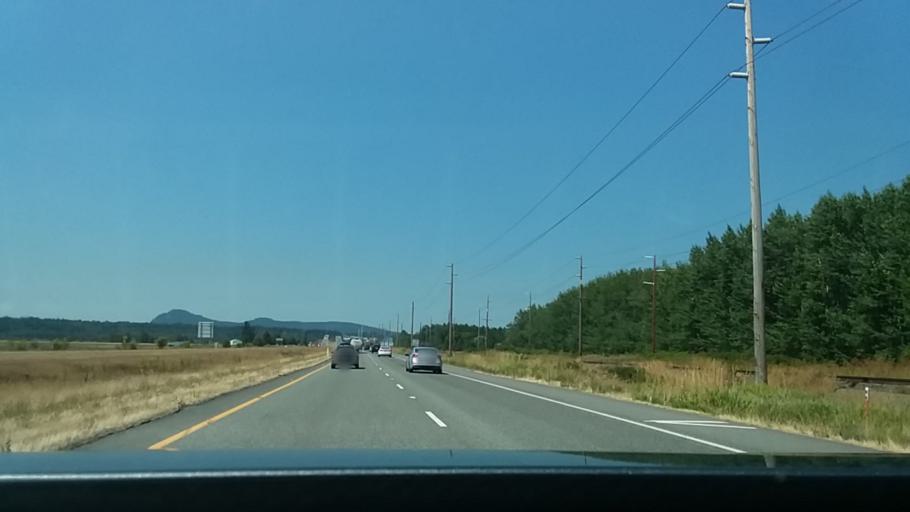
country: US
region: Washington
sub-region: Skagit County
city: Anacortes
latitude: 48.4506
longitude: -122.4866
